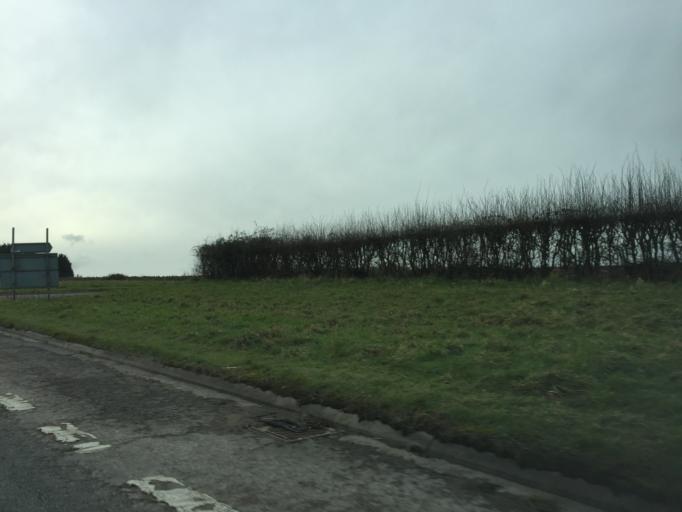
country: GB
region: England
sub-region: South Gloucestershire
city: Tytherington
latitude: 51.6124
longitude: -2.4850
